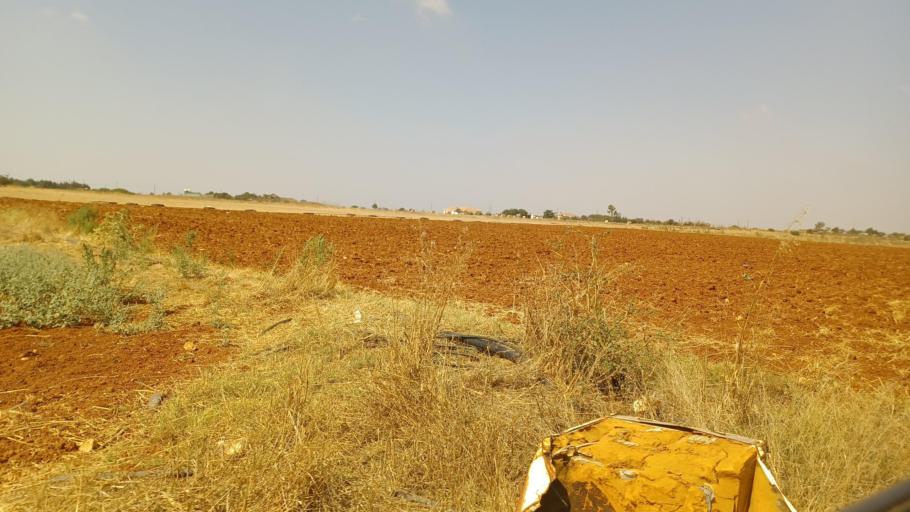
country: CY
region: Ammochostos
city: Frenaros
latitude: 35.0623
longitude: 33.9114
